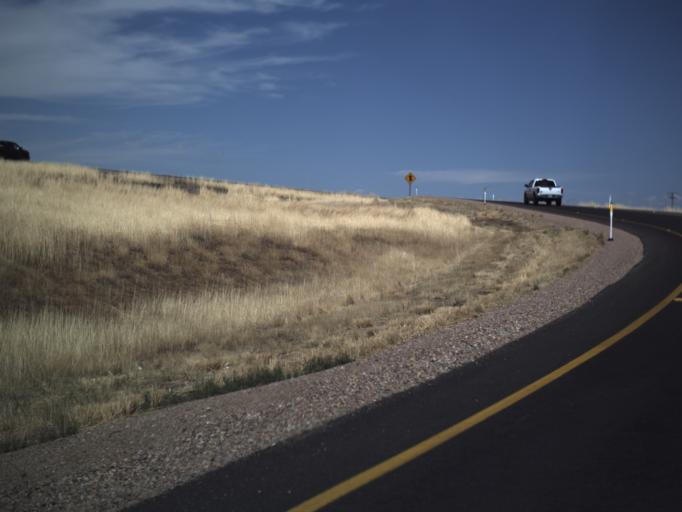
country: US
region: Utah
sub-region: Millard County
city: Fillmore
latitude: 38.8931
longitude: -112.4111
